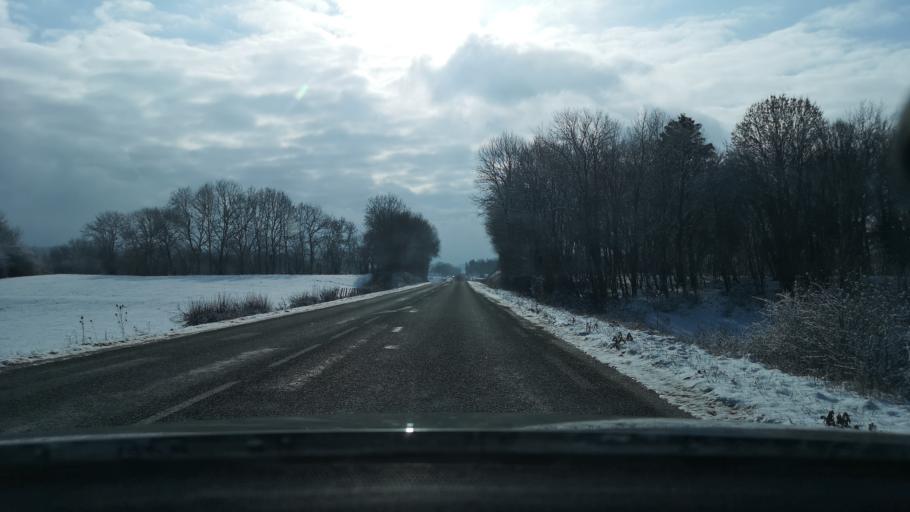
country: FR
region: Franche-Comte
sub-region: Departement du Jura
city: Orgelet
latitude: 46.5638
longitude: 5.5951
